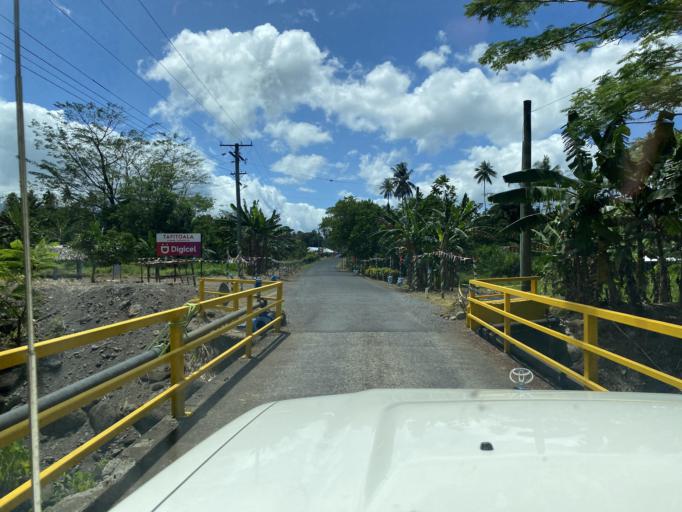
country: WS
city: Lotofaga
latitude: -14.0031
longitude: -171.8094
